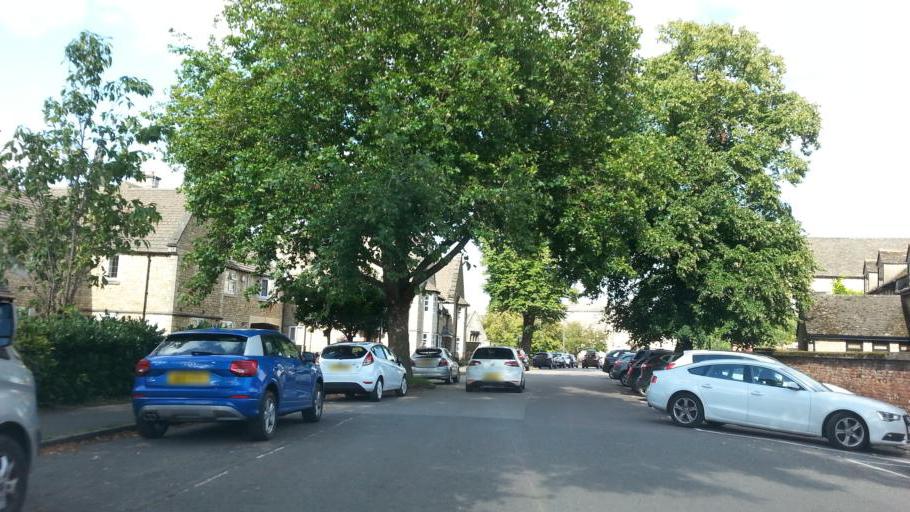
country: GB
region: England
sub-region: Lincolnshire
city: Stamford
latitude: 52.6495
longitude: -0.4799
